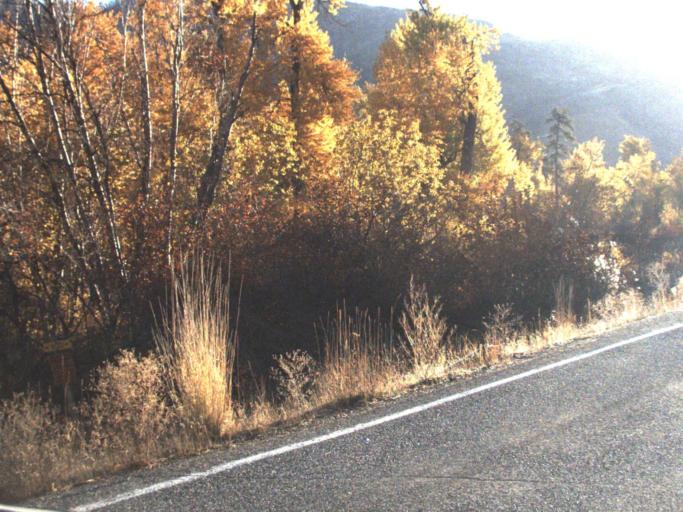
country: US
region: Washington
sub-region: Ferry County
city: Republic
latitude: 48.2690
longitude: -118.7029
